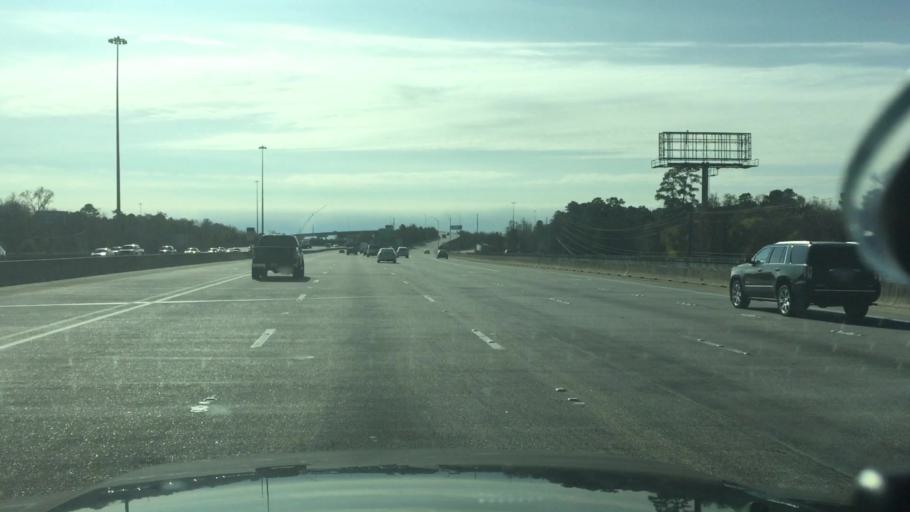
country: US
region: Texas
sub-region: Harris County
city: Spring
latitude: 30.1118
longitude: -95.4371
